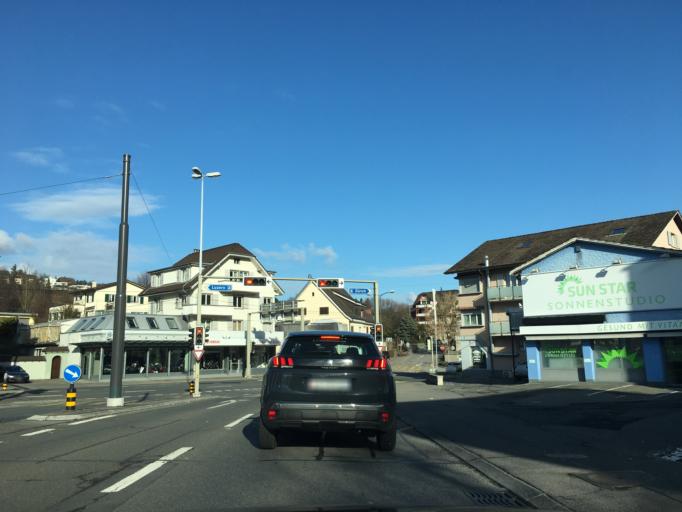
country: CH
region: Lucerne
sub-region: Lucerne-Land District
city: Ebikon
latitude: 47.0790
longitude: 8.3374
